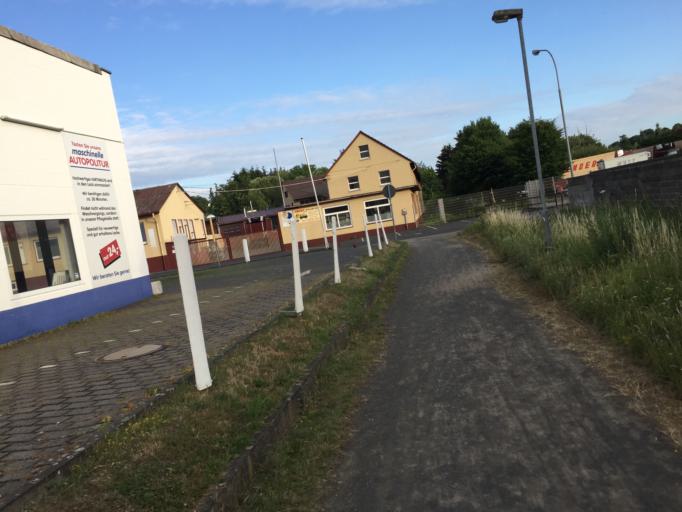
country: DE
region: Hesse
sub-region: Regierungsbezirk Giessen
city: Reiskirchen
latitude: 50.5982
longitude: 8.8274
